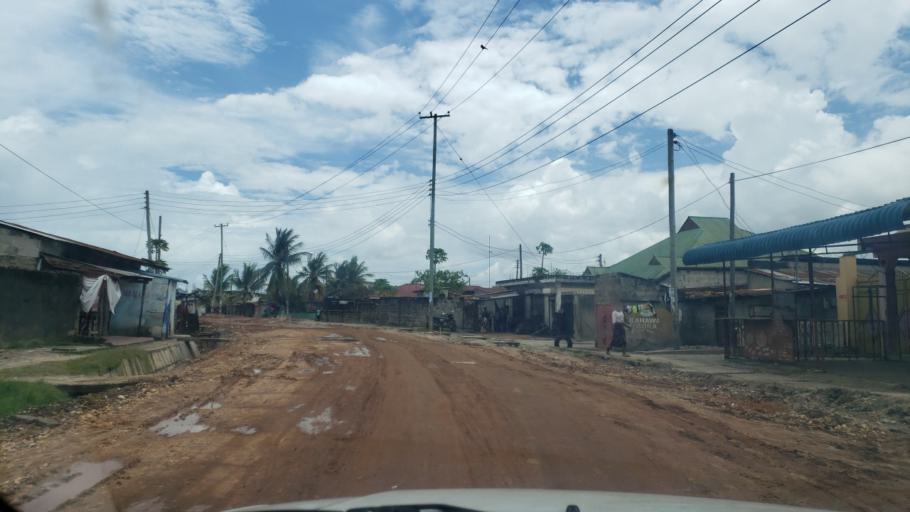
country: TZ
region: Dar es Salaam
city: Magomeni
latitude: -6.8075
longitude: 39.2335
